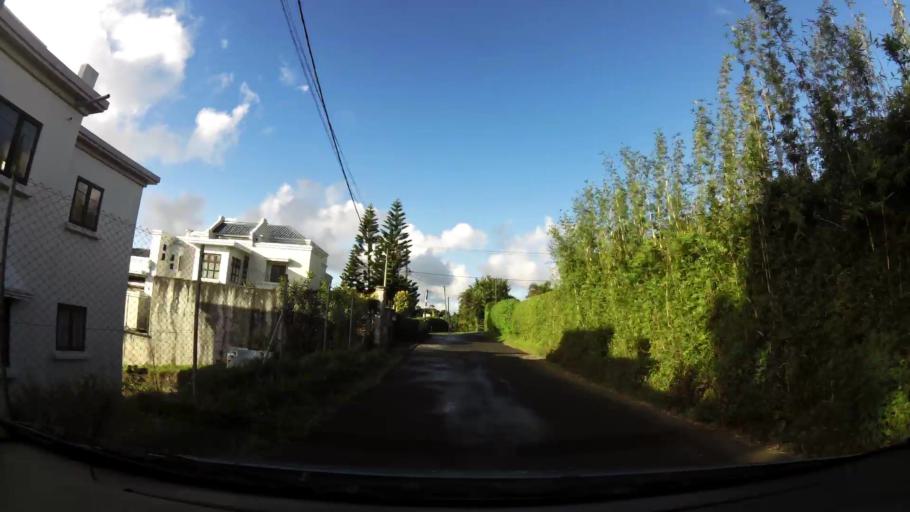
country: MU
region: Plaines Wilhems
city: Curepipe
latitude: -20.3172
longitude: 57.5053
